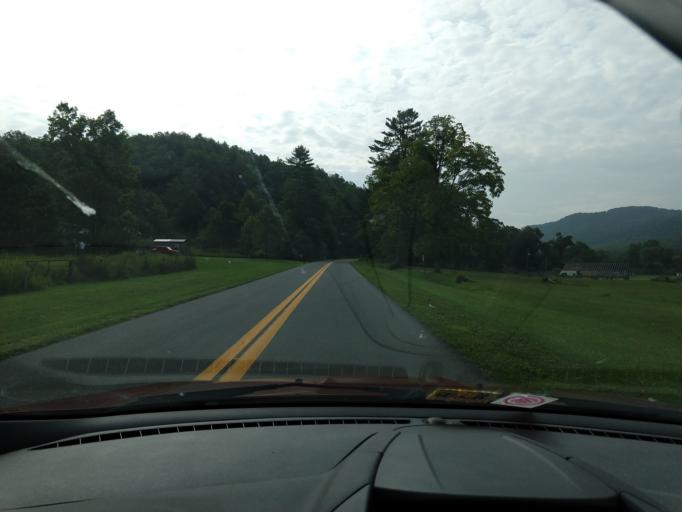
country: US
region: Virginia
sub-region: City of Covington
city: Covington
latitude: 37.9650
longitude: -80.1269
